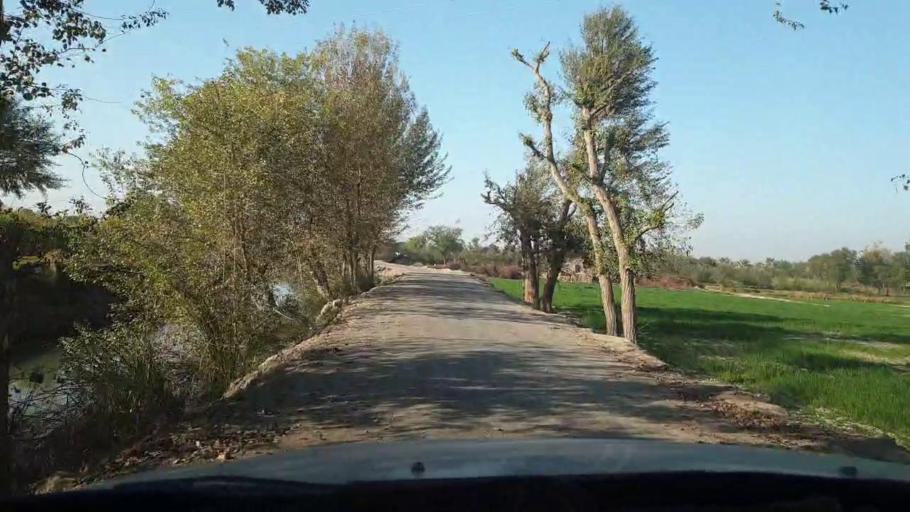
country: PK
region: Sindh
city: Adilpur
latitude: 27.9359
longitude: 69.2603
